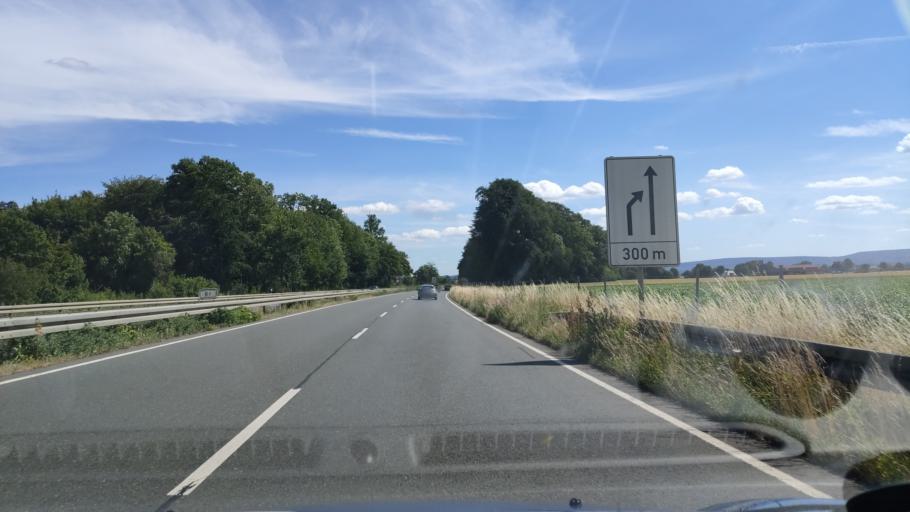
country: DE
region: Lower Saxony
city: Ronnenberg
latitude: 52.3400
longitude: 9.6435
